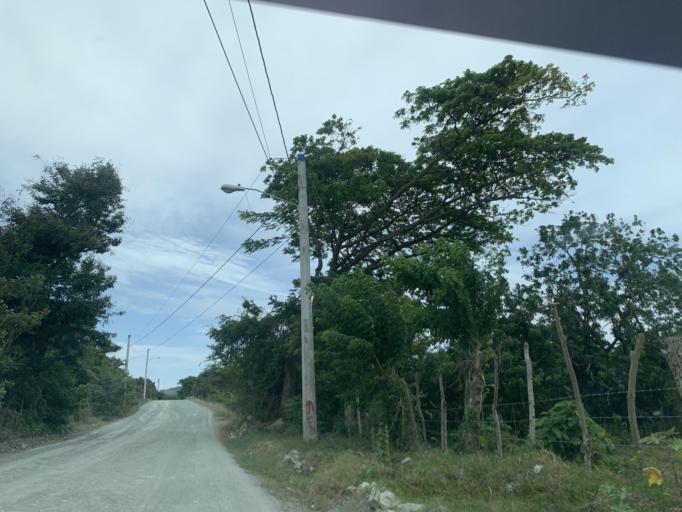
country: DO
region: Puerto Plata
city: Imbert
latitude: 19.8239
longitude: -70.7847
